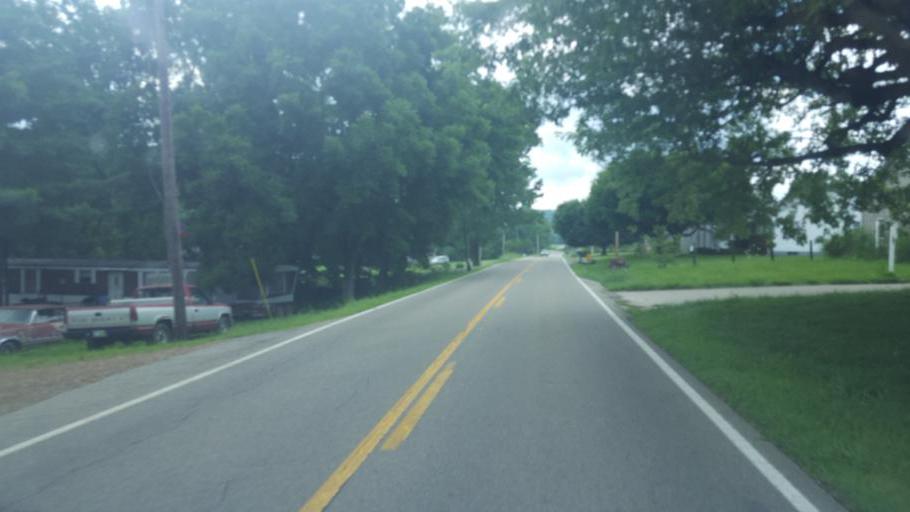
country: US
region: Ohio
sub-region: Ross County
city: Kingston
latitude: 39.4583
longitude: -82.7510
